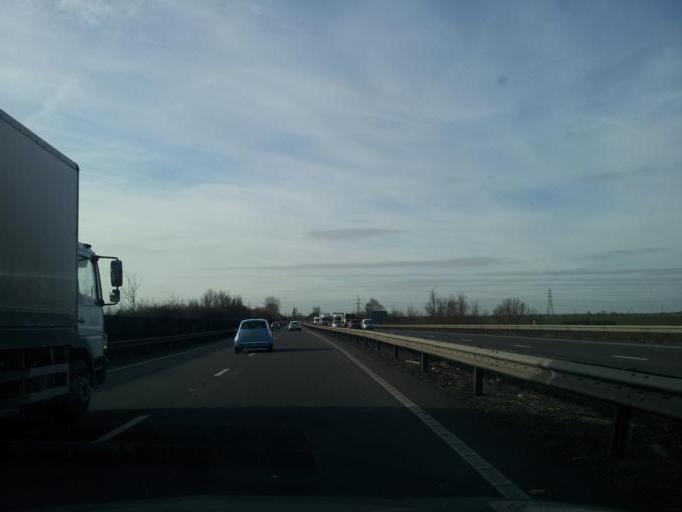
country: GB
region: England
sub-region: Cambridgeshire
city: Eaton Socon
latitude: 52.2288
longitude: -0.2929
